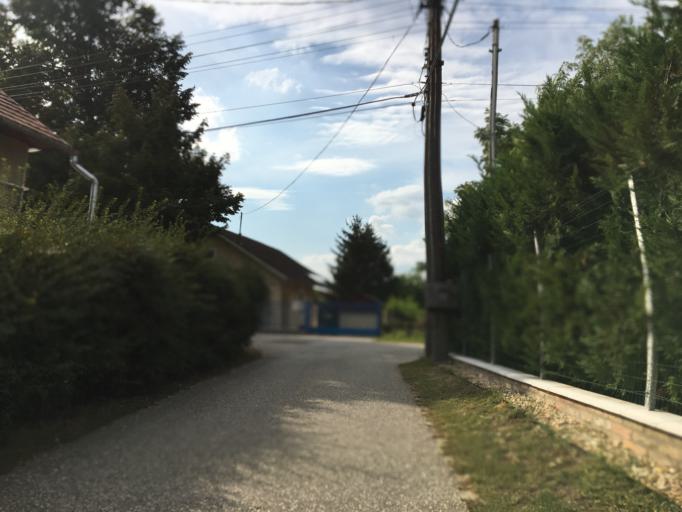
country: HU
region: Pest
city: Szigetszentmiklos
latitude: 47.3331
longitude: 19.0430
